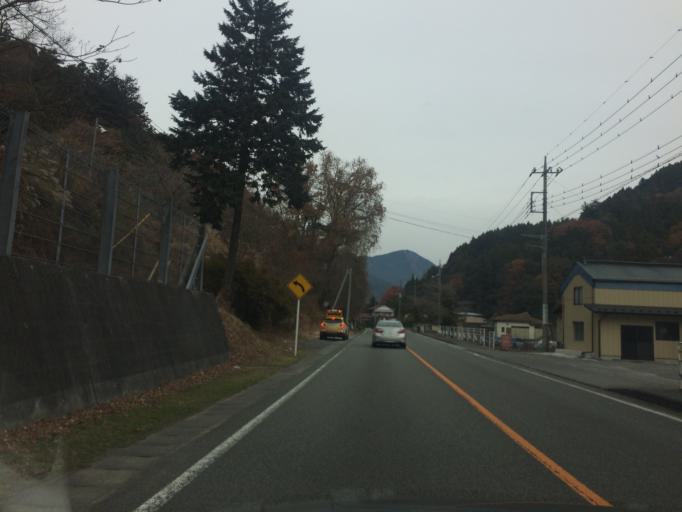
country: JP
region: Shizuoka
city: Fujinomiya
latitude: 35.3322
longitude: 138.4266
